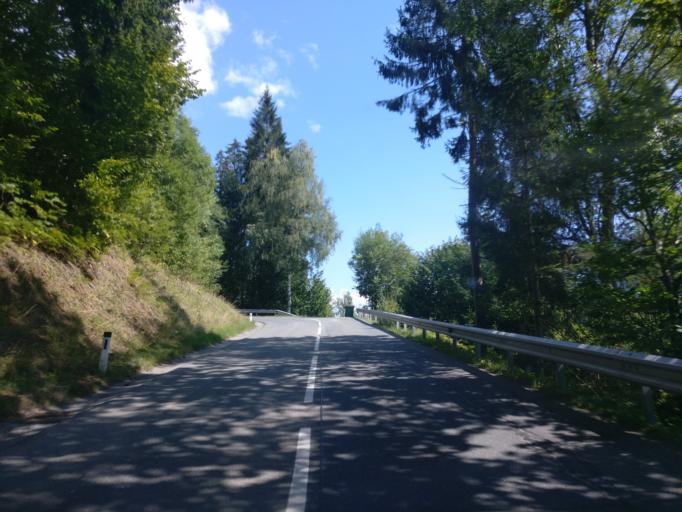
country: AT
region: Salzburg
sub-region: Politischer Bezirk Sankt Johann im Pongau
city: Muhlbach am Hochkonig
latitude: 47.3793
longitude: 13.1316
